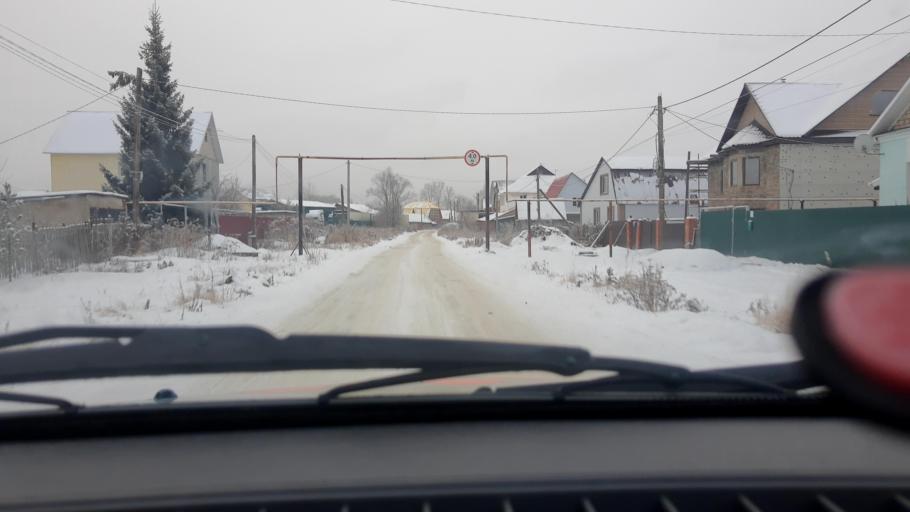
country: RU
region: Bashkortostan
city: Ufa
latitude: 54.8314
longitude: 56.1798
